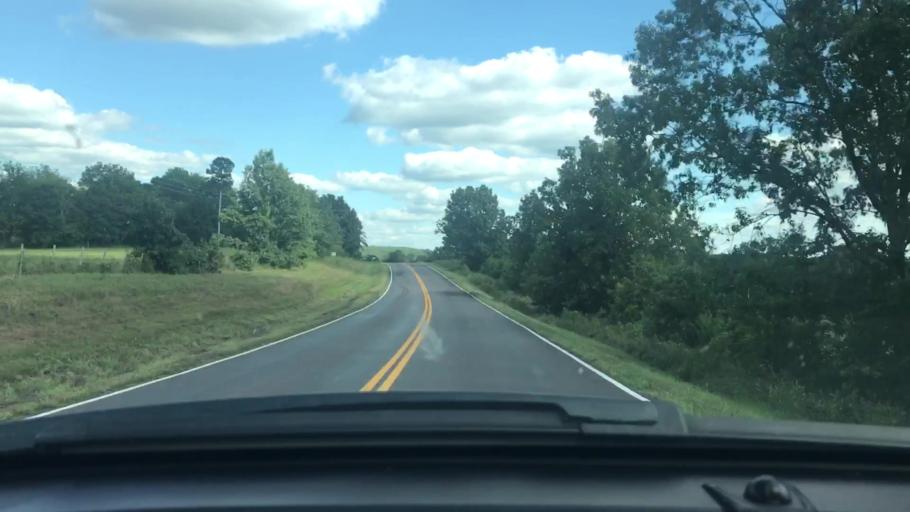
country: US
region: Missouri
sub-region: Wright County
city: Hartville
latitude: 37.3512
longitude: -92.3365
